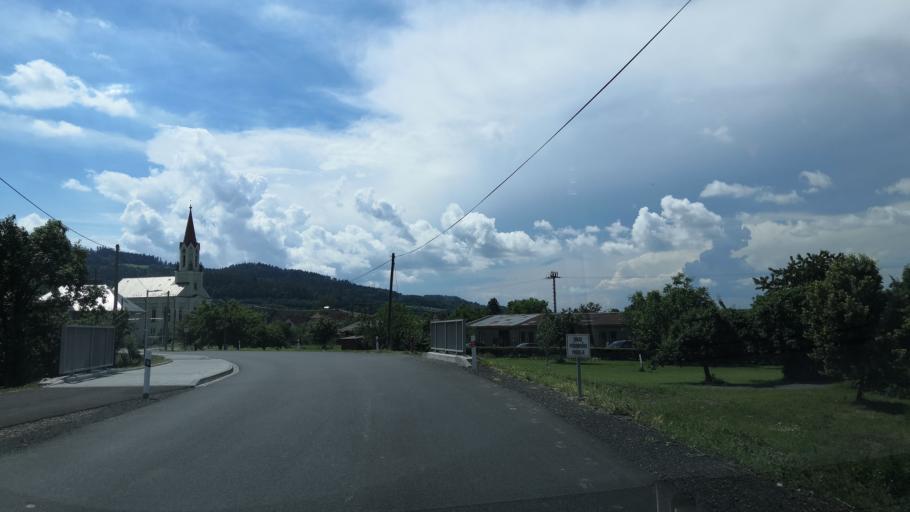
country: CZ
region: Zlin
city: Zasova
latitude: 49.4574
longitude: 18.0663
